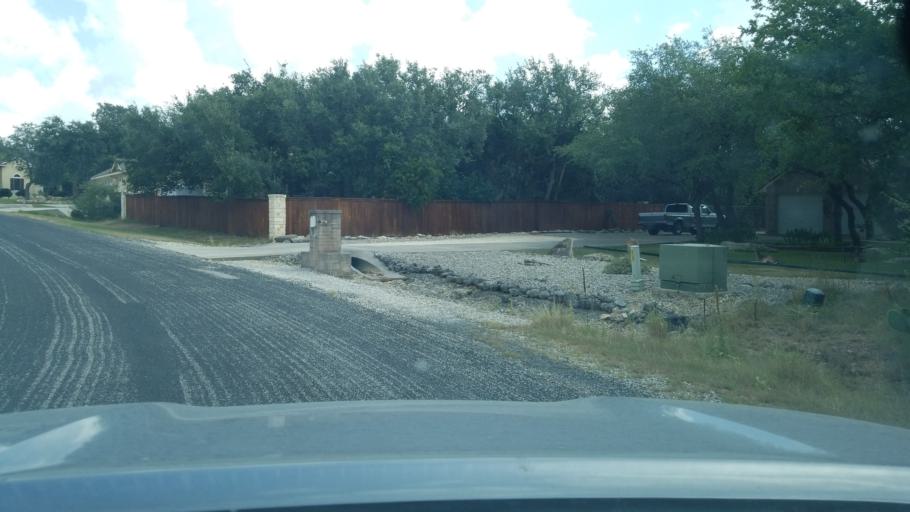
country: US
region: Texas
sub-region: Bexar County
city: Timberwood Park
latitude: 29.6922
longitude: -98.5027
